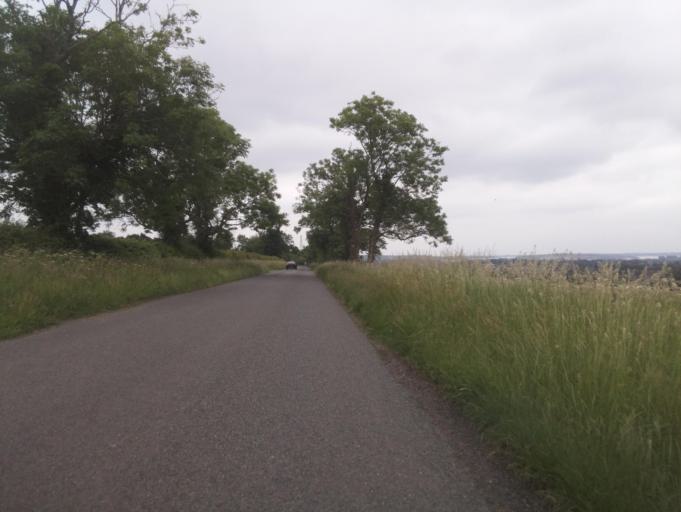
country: GB
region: England
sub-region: District of Rutland
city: Langham
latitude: 52.6702
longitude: -0.7566
